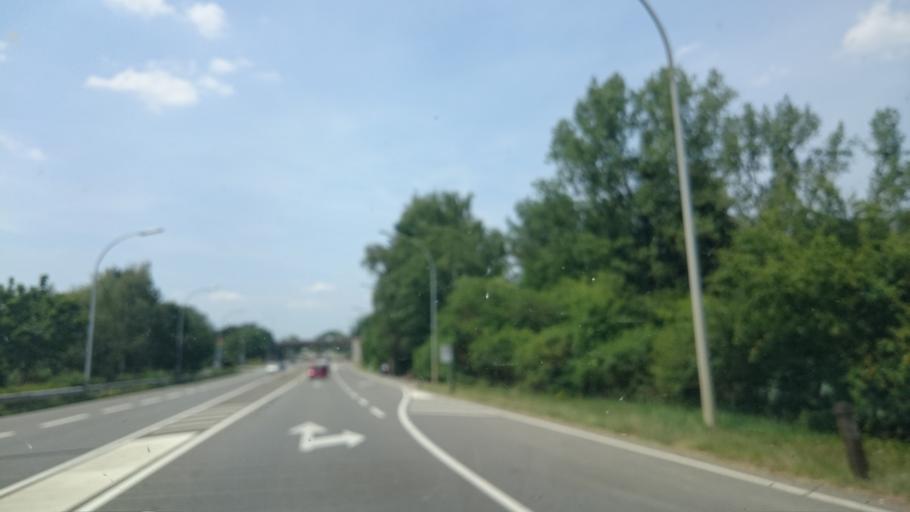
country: LU
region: Luxembourg
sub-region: Canton de Capellen
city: Mamer
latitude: 49.6371
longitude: 6.0109
